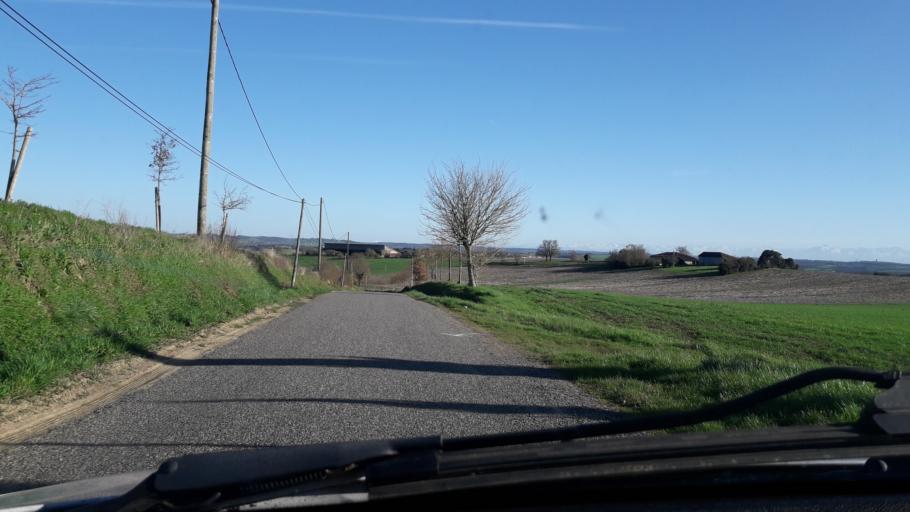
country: FR
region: Midi-Pyrenees
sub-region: Departement du Gers
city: Samatan
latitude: 43.5839
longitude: 1.0008
